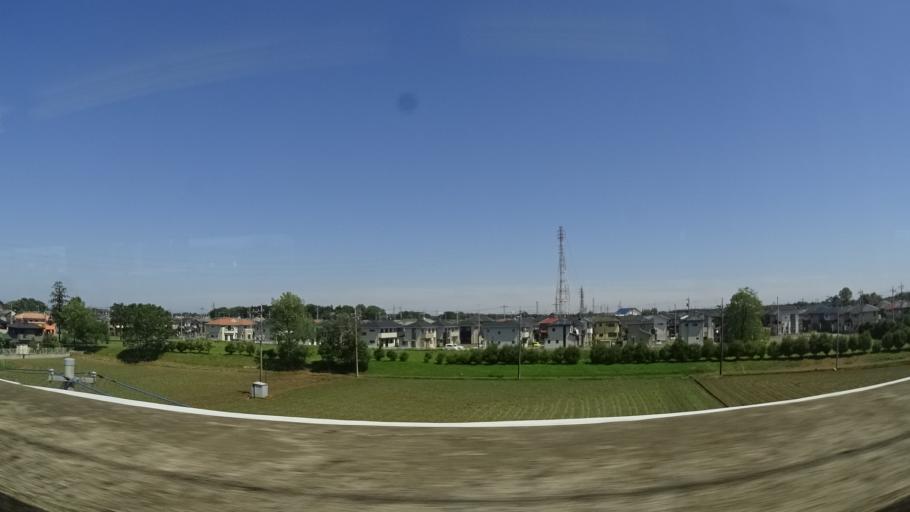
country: JP
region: Ibaraki
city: Koga
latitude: 36.1873
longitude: 139.7424
